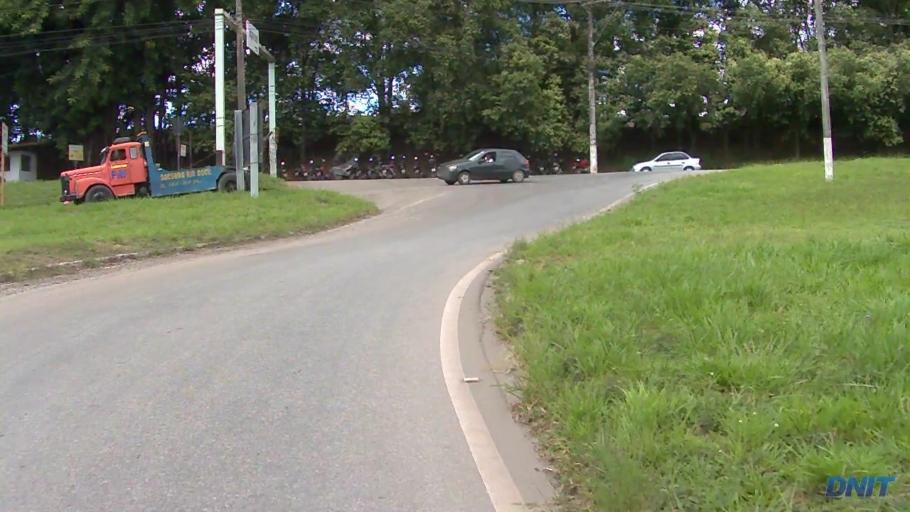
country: BR
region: Minas Gerais
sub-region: Coronel Fabriciano
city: Coronel Fabriciano
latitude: -19.5276
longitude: -42.6402
